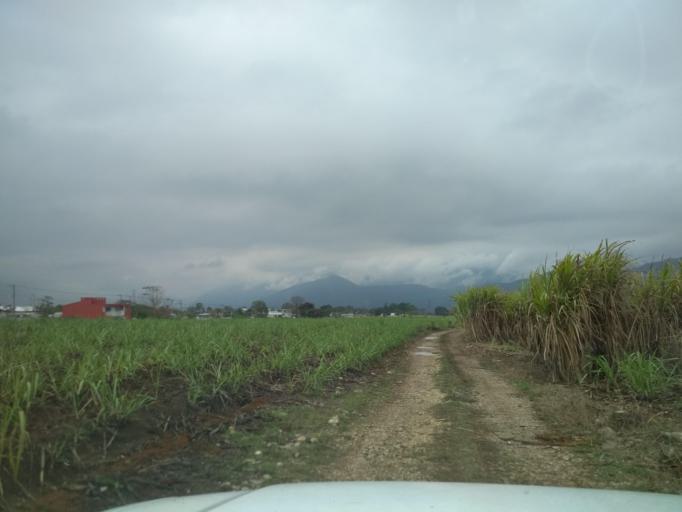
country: MX
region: Veracruz
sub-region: Cordoba
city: San Jose de Tapia
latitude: 18.8475
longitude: -96.9691
